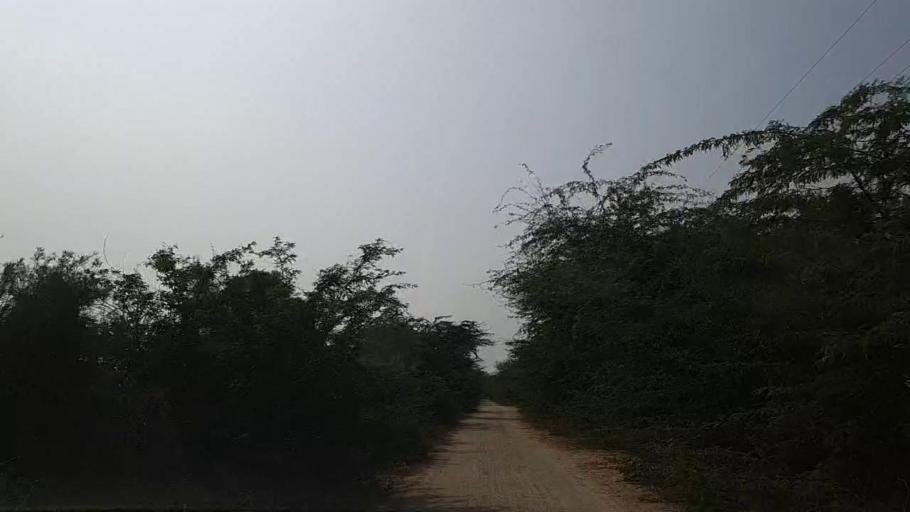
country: PK
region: Sindh
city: Mirpur Sakro
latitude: 24.6097
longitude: 67.7277
